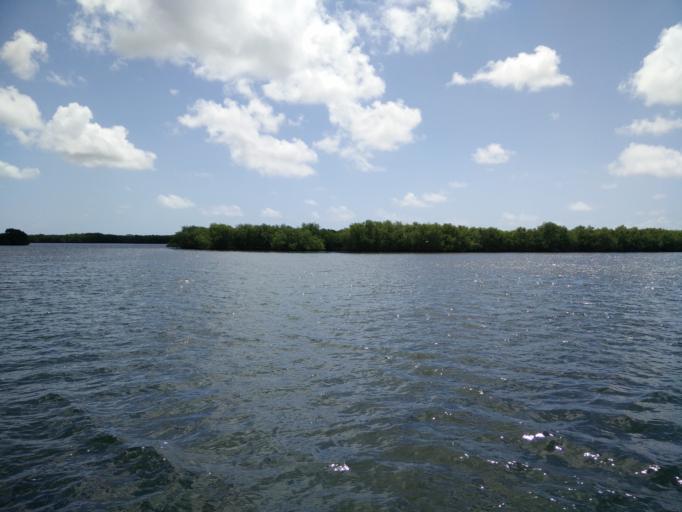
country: GP
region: Guadeloupe
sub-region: Guadeloupe
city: Petit-Canal
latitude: 16.3557
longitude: -61.5012
